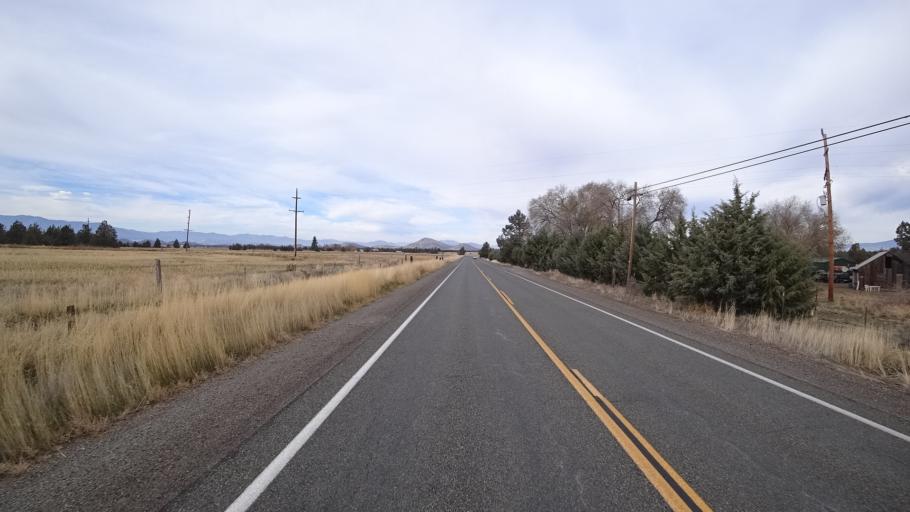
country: US
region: California
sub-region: Siskiyou County
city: Montague
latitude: 41.6187
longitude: -122.3740
